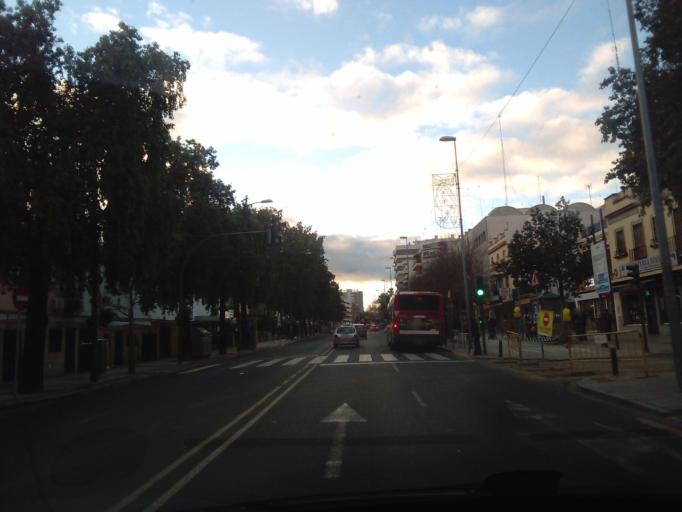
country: ES
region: Andalusia
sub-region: Provincia de Sevilla
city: Sevilla
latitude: 37.3813
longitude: -5.9626
